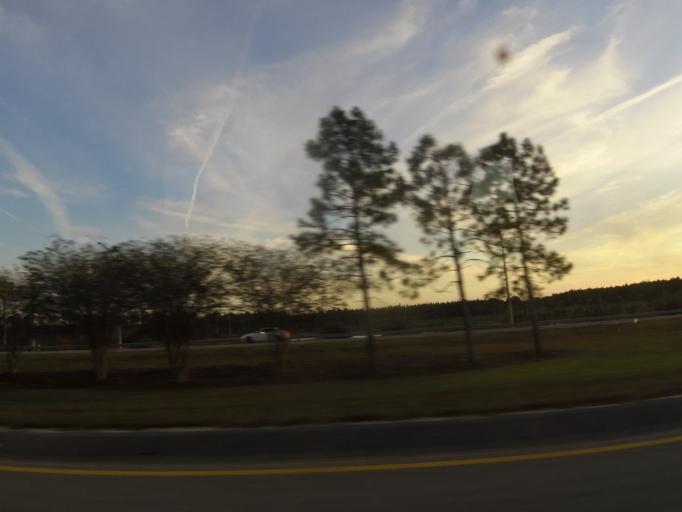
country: US
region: Florida
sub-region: Saint Johns County
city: Palm Valley
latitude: 30.1150
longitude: -81.4350
